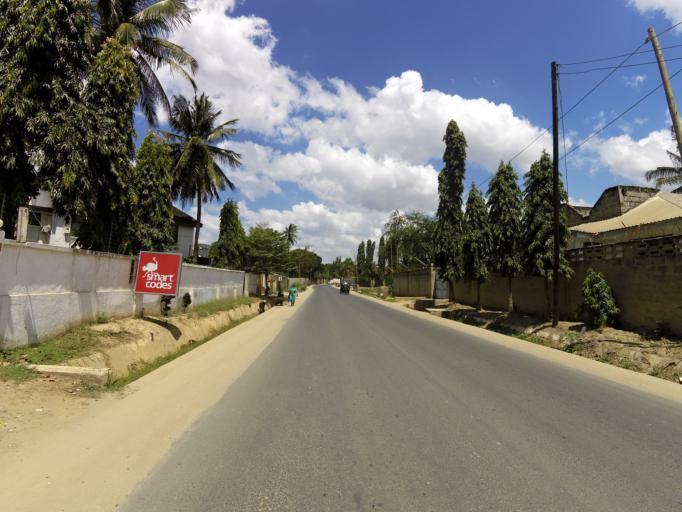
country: TZ
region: Dar es Salaam
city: Magomeni
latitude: -6.7688
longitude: 39.2509
